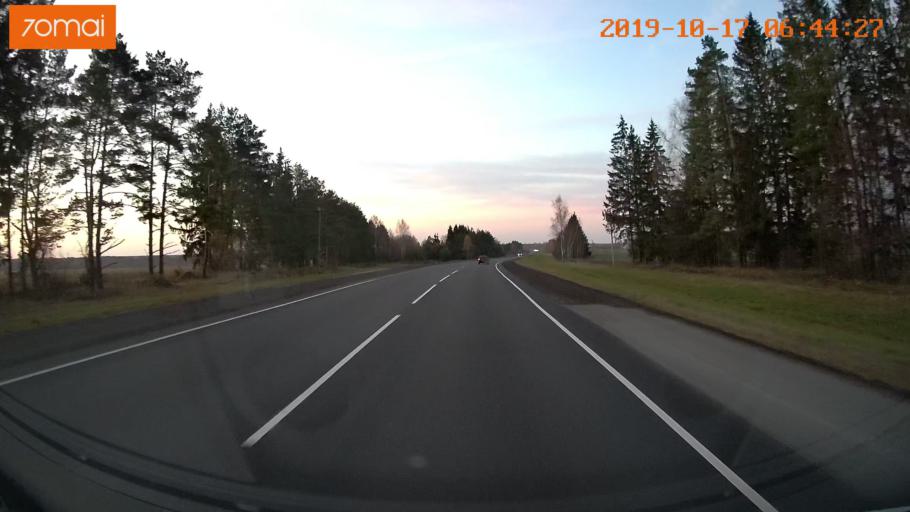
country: RU
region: Vladimir
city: Kideksha
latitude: 56.5724
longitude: 40.5543
